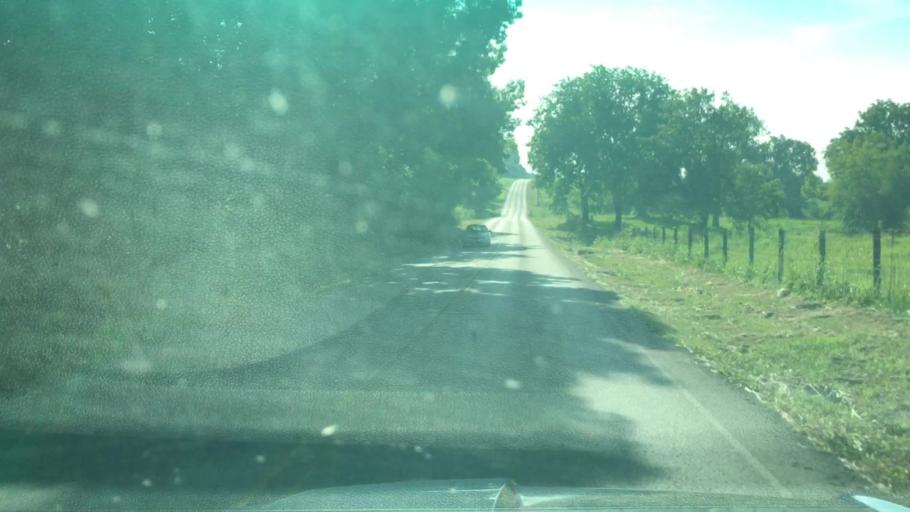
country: US
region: Tennessee
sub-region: Williamson County
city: Thompson's Station
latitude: 35.7907
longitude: -86.8738
